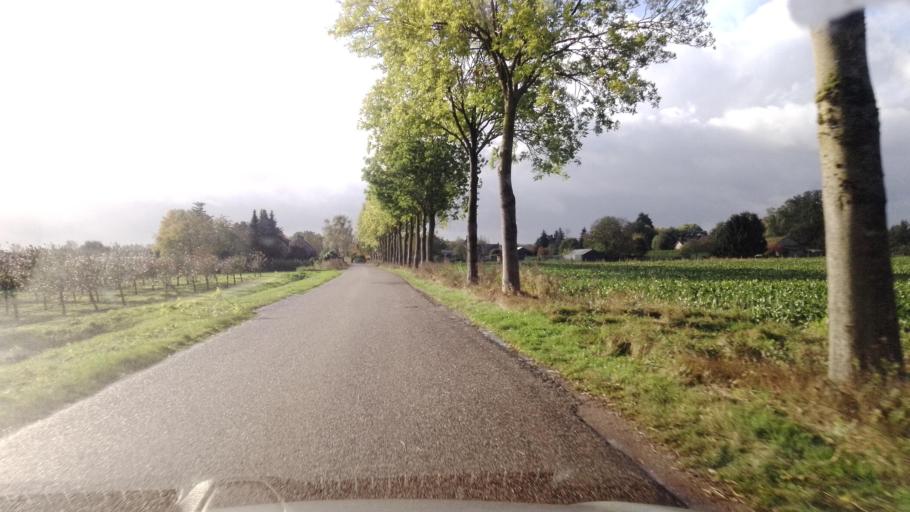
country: NL
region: Limburg
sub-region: Gemeente Peel en Maas
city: Maasbree
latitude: 51.3410
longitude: 6.0836
